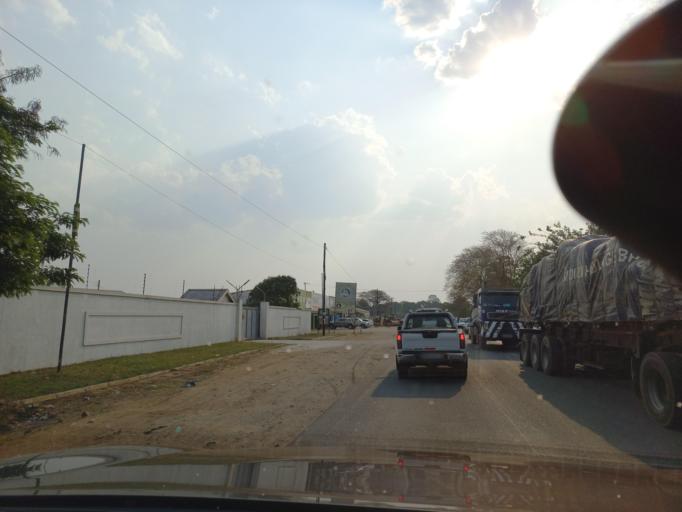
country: ZM
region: Lusaka
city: Lusaka
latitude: -15.4640
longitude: 28.2366
